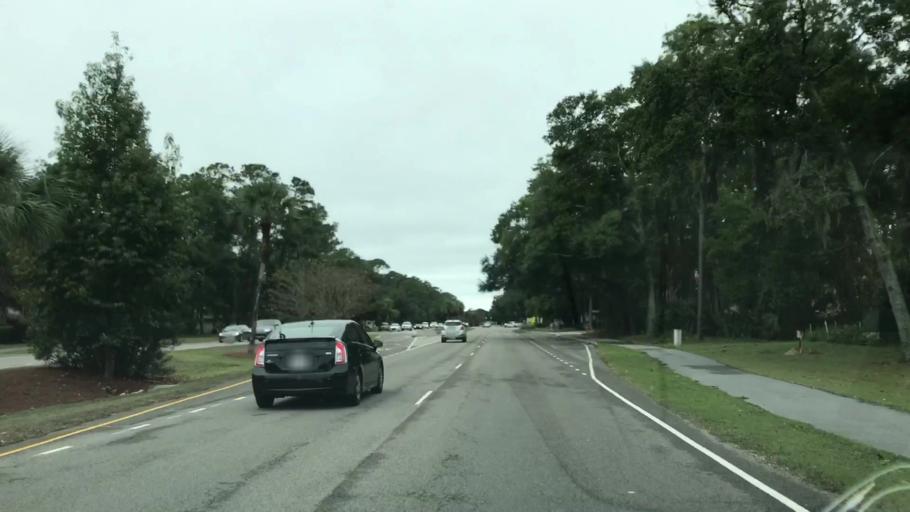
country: US
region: South Carolina
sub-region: Beaufort County
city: Hilton Head Island
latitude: 32.1752
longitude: -80.7317
